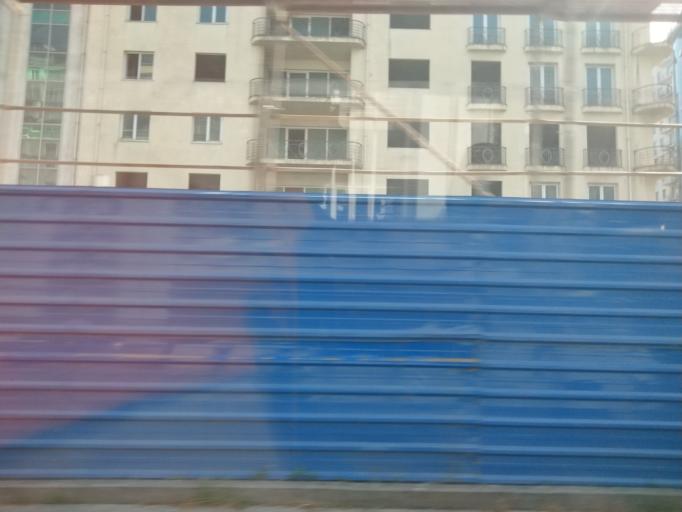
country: GE
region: Ajaria
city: Batumi
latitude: 41.6442
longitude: 41.6177
